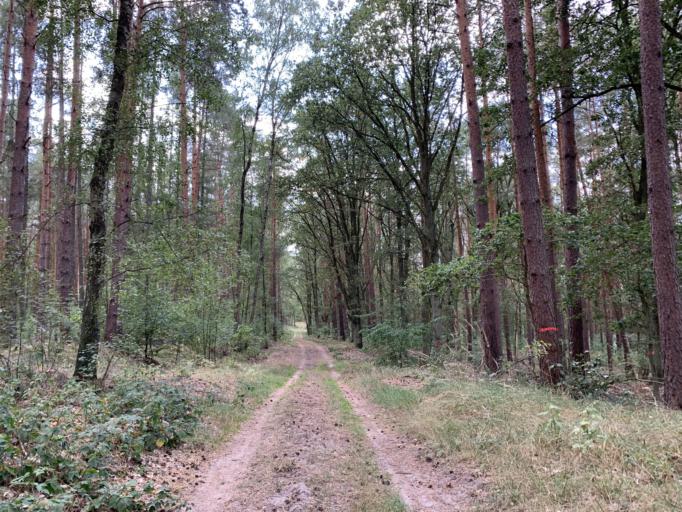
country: DE
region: Brandenburg
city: Michendorf
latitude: 52.3159
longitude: 12.9885
